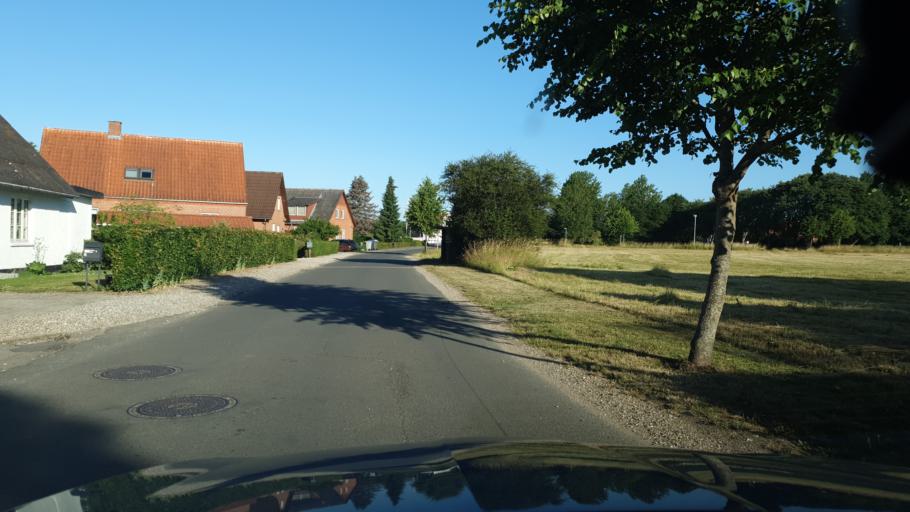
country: DK
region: Zealand
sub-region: Soro Kommune
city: Frederiksberg
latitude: 55.4006
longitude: 11.5643
